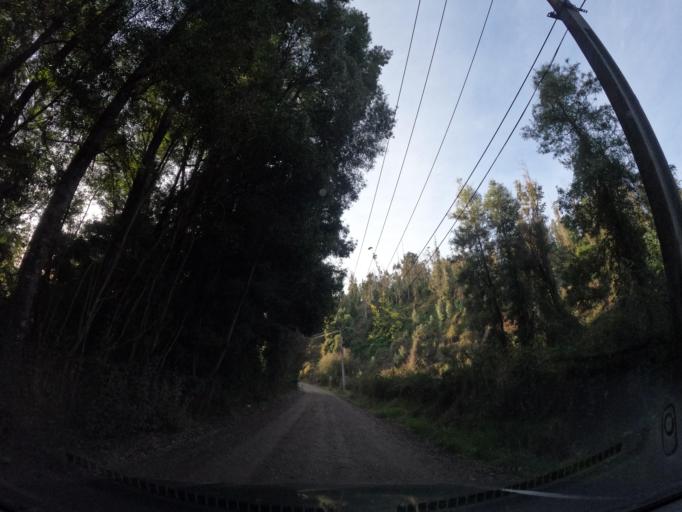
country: CL
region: Biobio
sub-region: Provincia de Concepcion
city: Chiguayante
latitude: -36.8689
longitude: -72.9954
